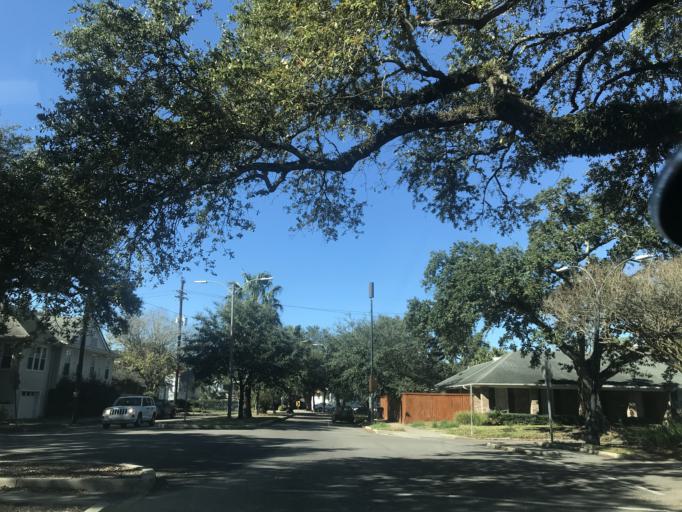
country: US
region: Louisiana
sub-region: Orleans Parish
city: New Orleans
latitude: 29.9525
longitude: -90.1125
